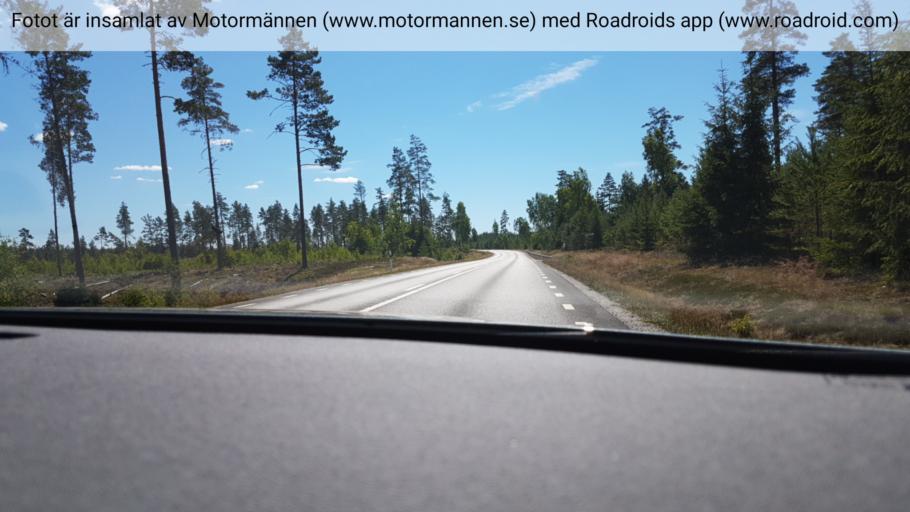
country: SE
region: Joenkoeping
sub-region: Gnosjo Kommun
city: Gnosjoe
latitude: 57.5328
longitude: 13.6867
